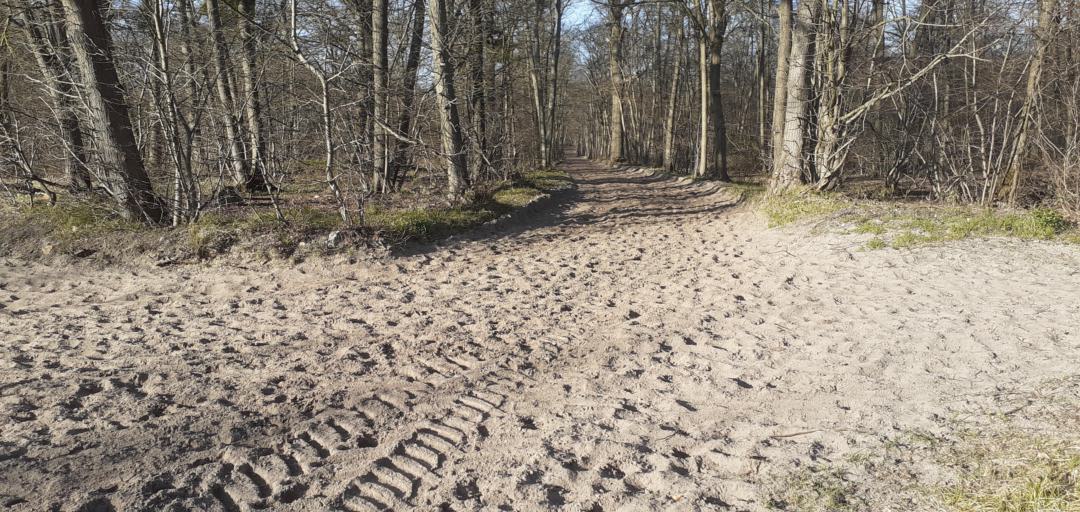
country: FR
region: Picardie
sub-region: Departement de l'Oise
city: Coye-la-Foret
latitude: 49.1629
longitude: 2.4691
